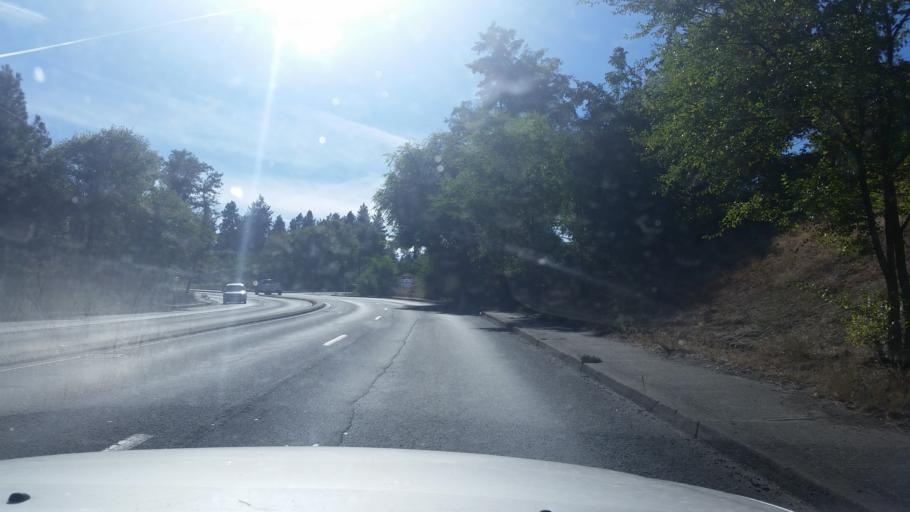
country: US
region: Washington
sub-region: Spokane County
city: Spokane
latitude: 47.6447
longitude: -117.3616
